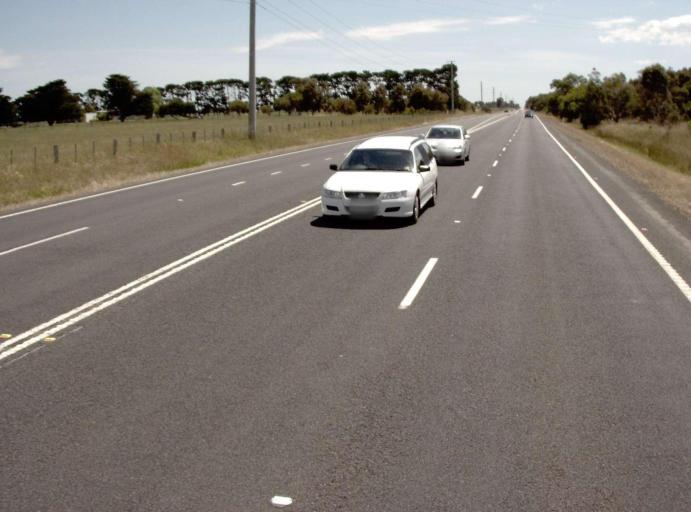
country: AU
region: Victoria
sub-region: Wellington
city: Sale
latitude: -38.1037
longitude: 146.9275
